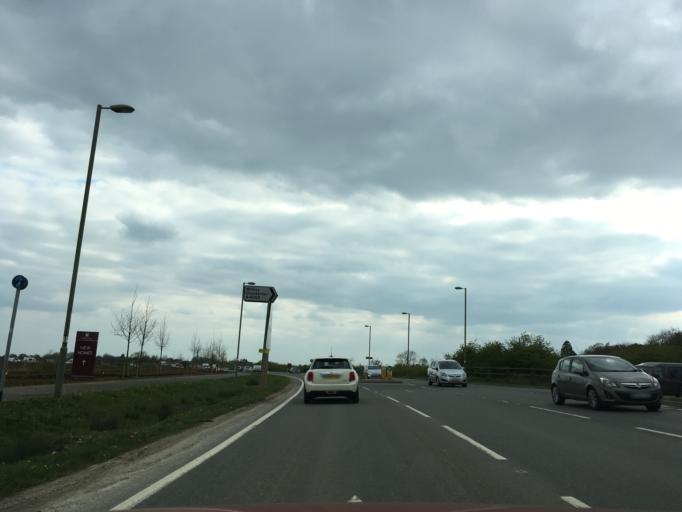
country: GB
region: England
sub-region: Oxfordshire
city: Bicester
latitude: 51.8989
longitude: -1.1828
